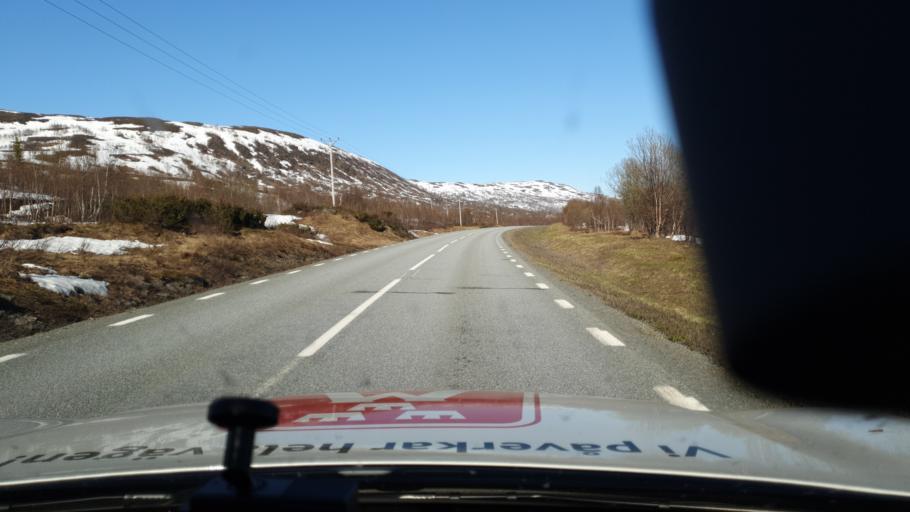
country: NO
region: Nordland
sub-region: Rana
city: Mo i Rana
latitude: 66.1226
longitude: 14.7134
